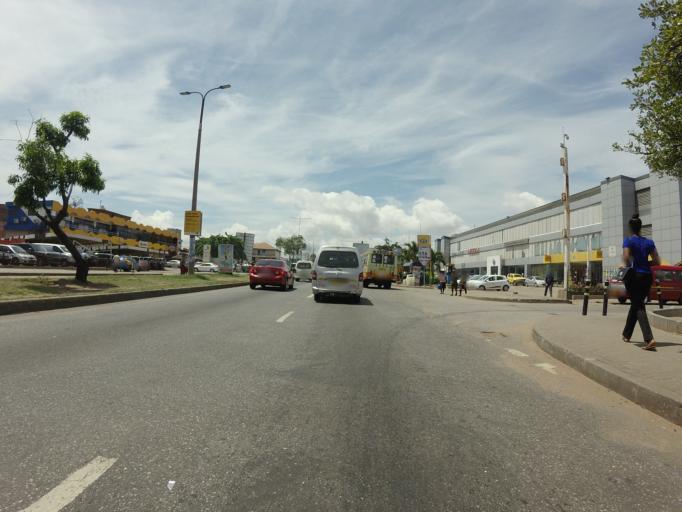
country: GH
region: Greater Accra
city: Accra
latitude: 5.5601
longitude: -0.2272
